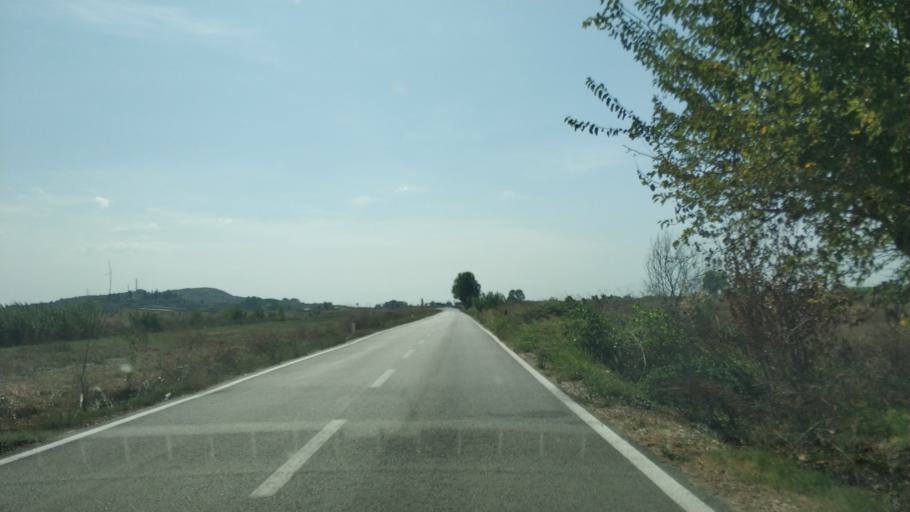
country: AL
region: Fier
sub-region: Rrethi i Fierit
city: Dermenas
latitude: 40.7440
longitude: 19.4844
